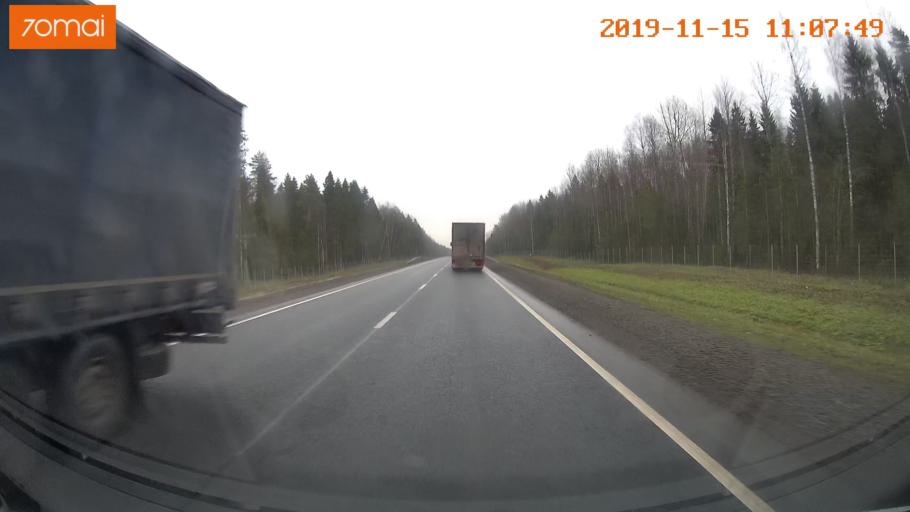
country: RU
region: Vologda
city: Chebsara
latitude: 59.1197
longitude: 39.0597
